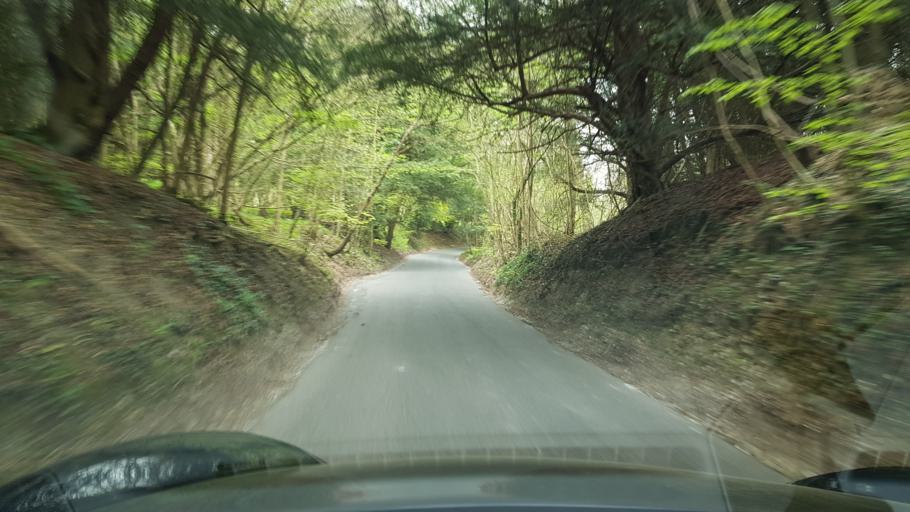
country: GB
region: England
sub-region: Surrey
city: East Horsley
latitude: 51.2280
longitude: -0.4057
